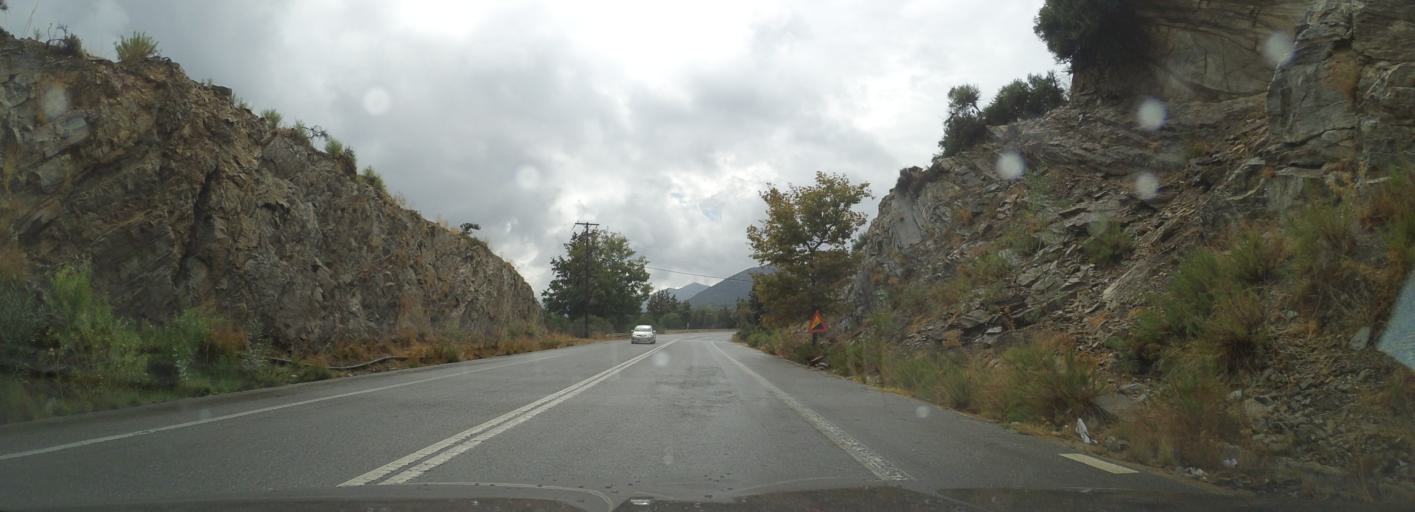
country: GR
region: Crete
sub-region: Nomos Irakleiou
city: Tilisos
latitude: 35.3948
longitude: 24.9491
